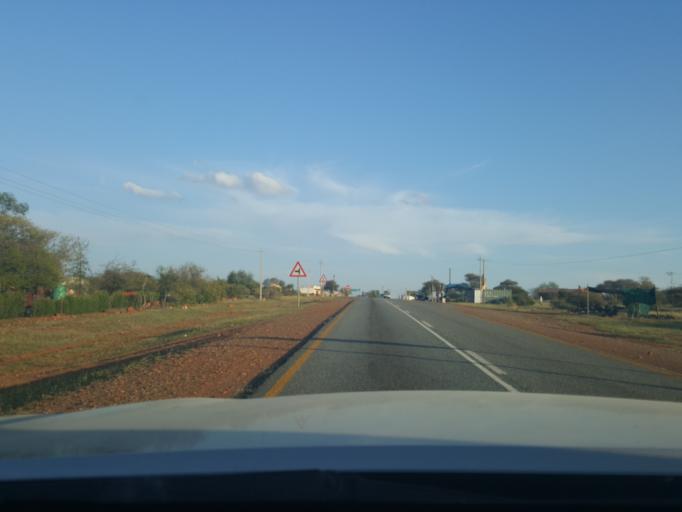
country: ZA
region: North-West
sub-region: Ngaka Modiri Molema District Municipality
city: Zeerust
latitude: -25.3844
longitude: 26.0838
